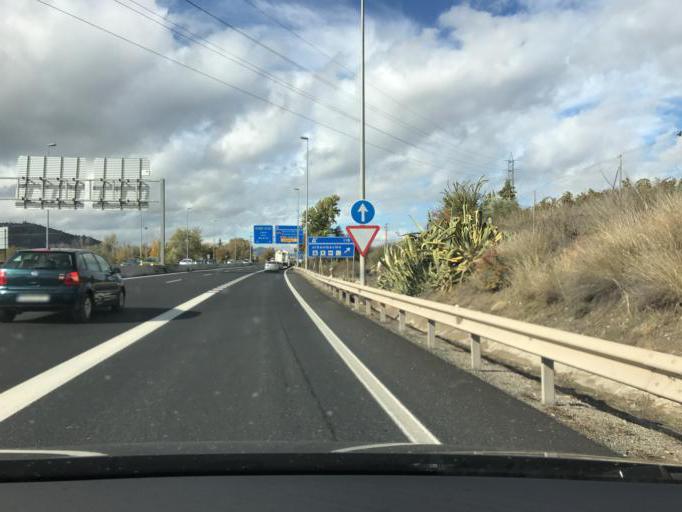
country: ES
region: Andalusia
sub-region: Provincia de Granada
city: Albolote
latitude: 37.2375
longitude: -3.6474
